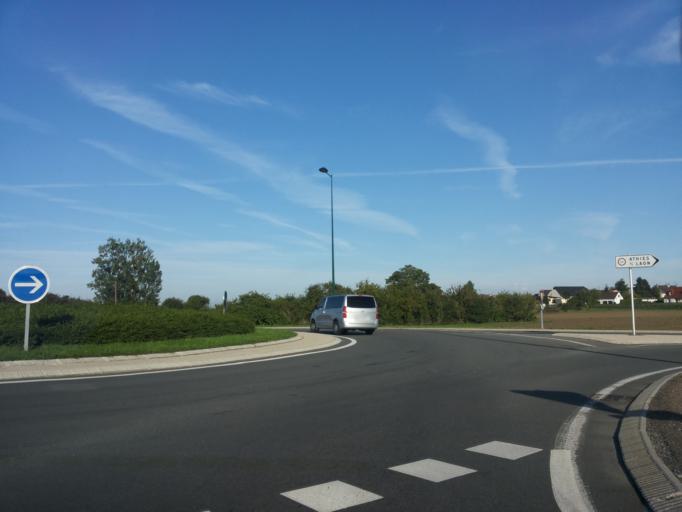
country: FR
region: Picardie
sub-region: Departement de l'Aisne
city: Athies-sous-Laon
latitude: 49.5630
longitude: 3.6866
